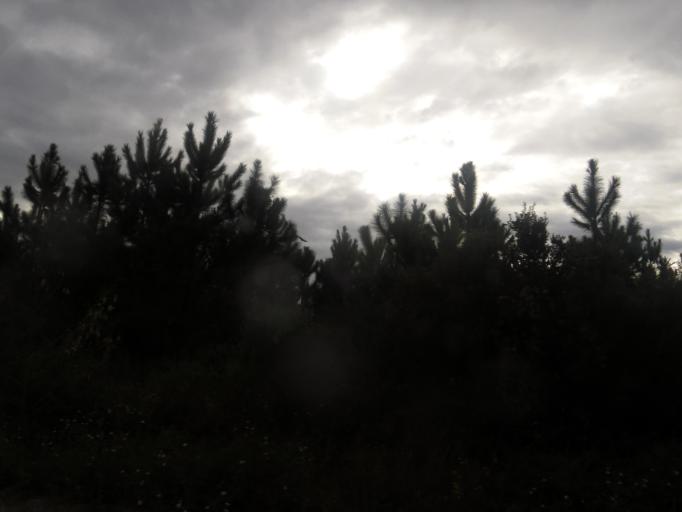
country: US
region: Florida
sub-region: Flagler County
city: Bunnell
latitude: 29.5295
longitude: -81.3168
